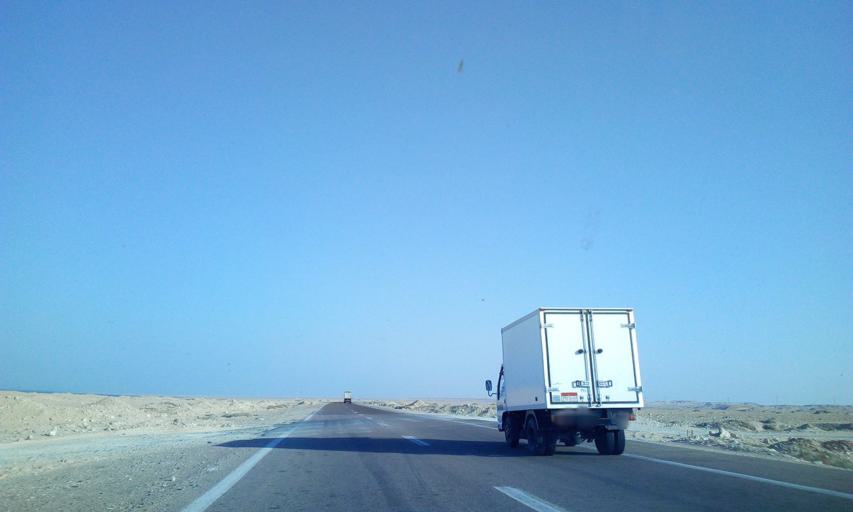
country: EG
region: As Suways
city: Ain Sukhna
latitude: 28.8331
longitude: 32.7115
